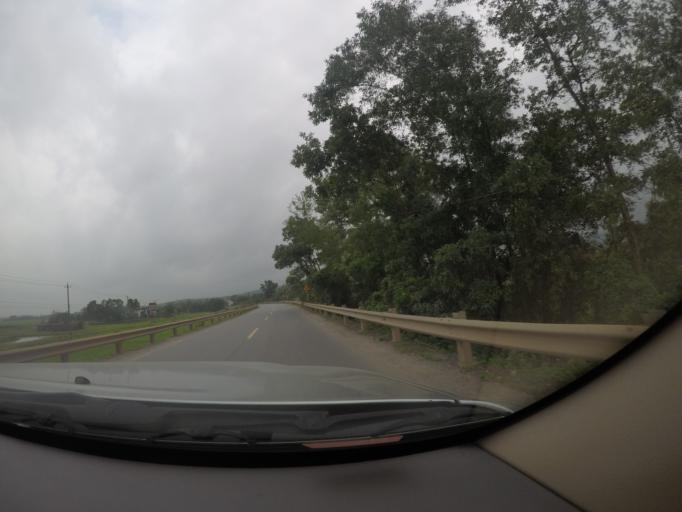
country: VN
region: Quang Binh
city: Kien Giang
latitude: 17.2074
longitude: 106.7155
